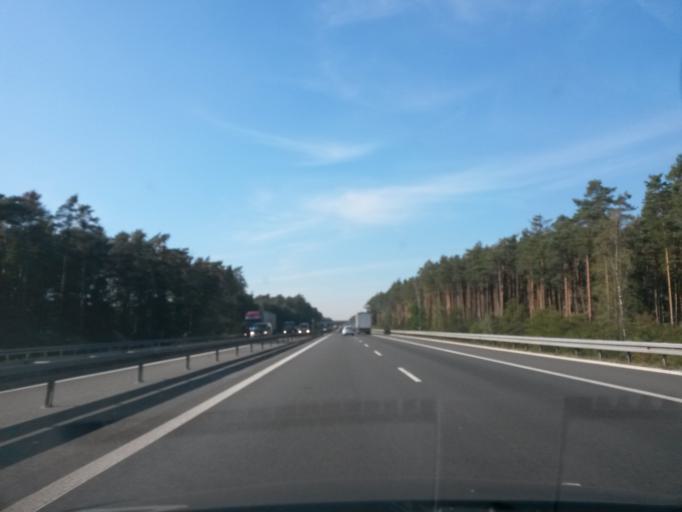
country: PL
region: Opole Voivodeship
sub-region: Powiat opolski
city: Komprachcice
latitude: 50.6183
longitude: 17.7654
